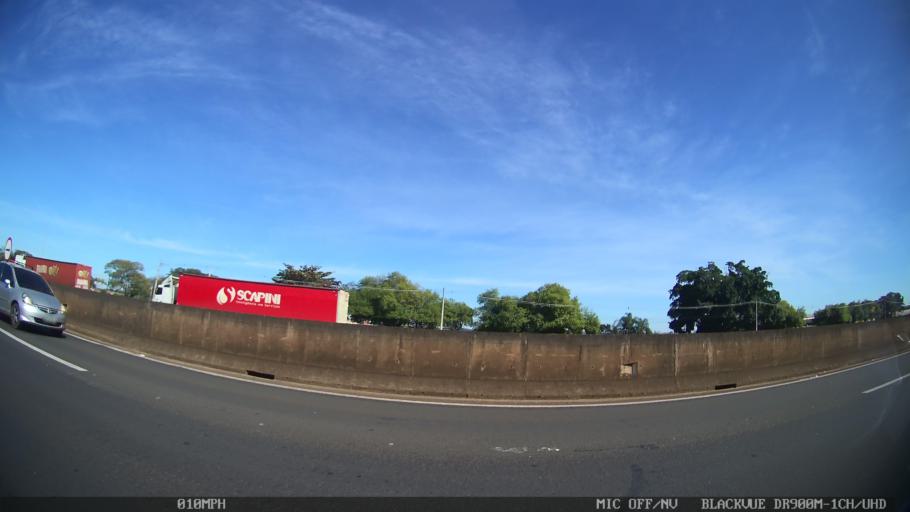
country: BR
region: Sao Paulo
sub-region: Leme
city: Leme
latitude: -22.2011
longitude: -47.3957
